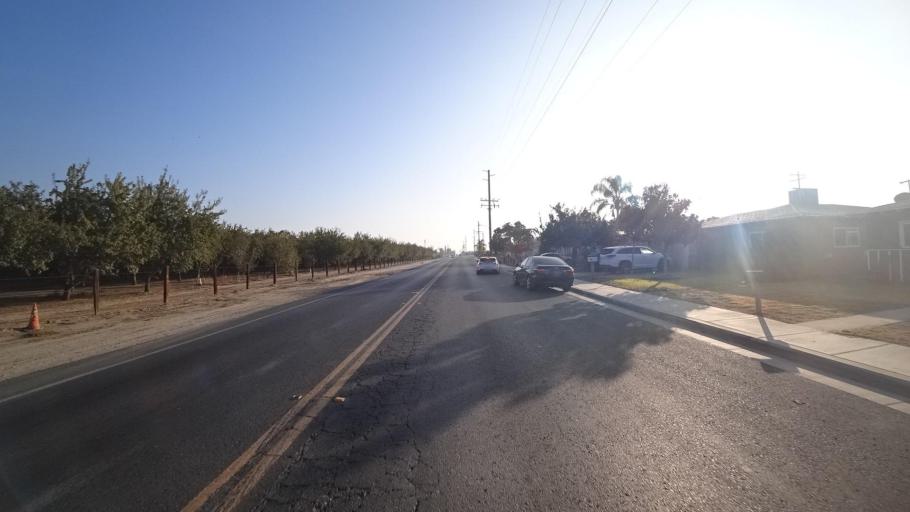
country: US
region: California
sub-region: Kern County
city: Delano
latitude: 35.7911
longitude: -119.2356
